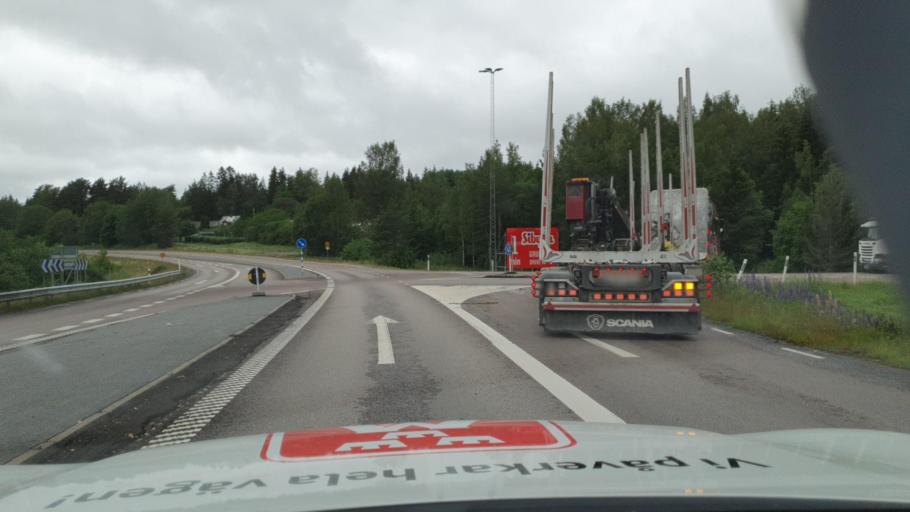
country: SE
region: Vaermland
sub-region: Karlstads Kommun
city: Valberg
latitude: 59.3718
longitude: 13.1398
